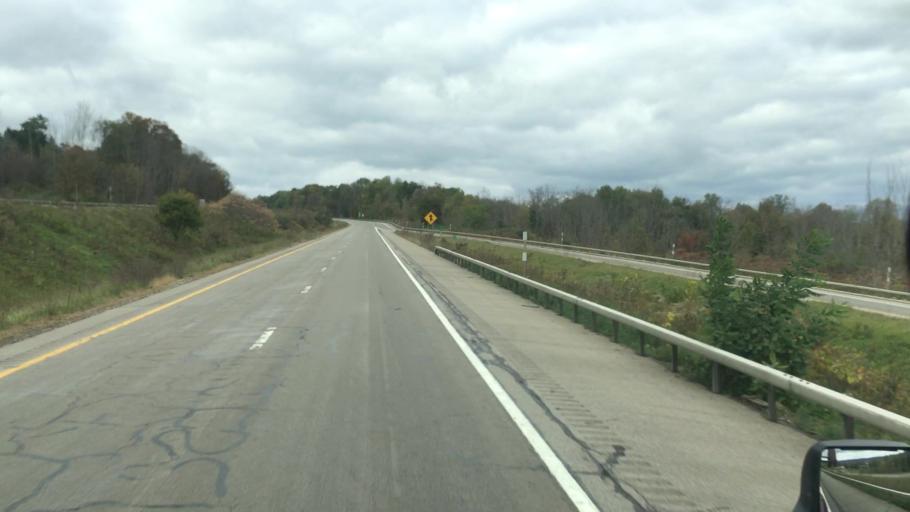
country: US
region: New York
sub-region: Cattaraugus County
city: Randolph
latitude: 42.1597
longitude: -78.9960
